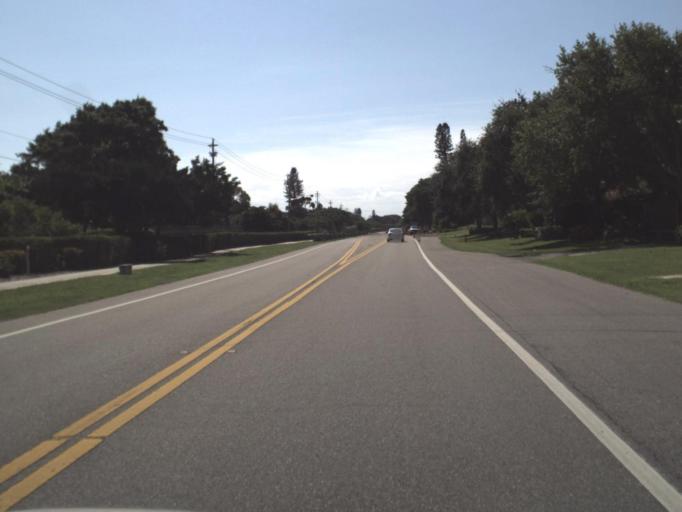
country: US
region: Florida
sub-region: Manatee County
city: Longboat Key
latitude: 27.4041
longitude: -82.6512
